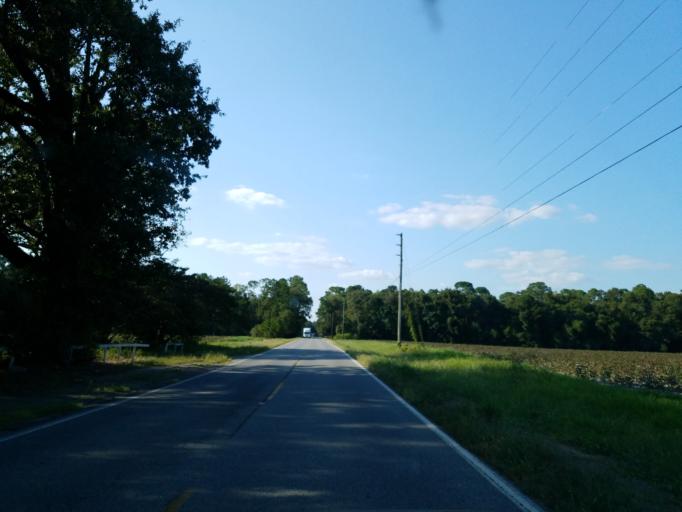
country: US
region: Georgia
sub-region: Cook County
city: Adel
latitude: 31.1015
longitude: -83.4108
